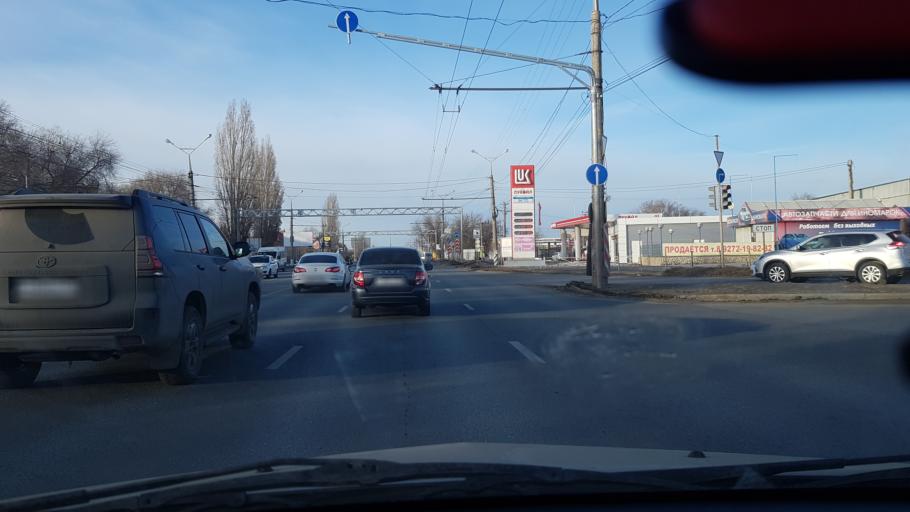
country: RU
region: Samara
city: Tol'yatti
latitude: 53.5357
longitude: 49.3944
